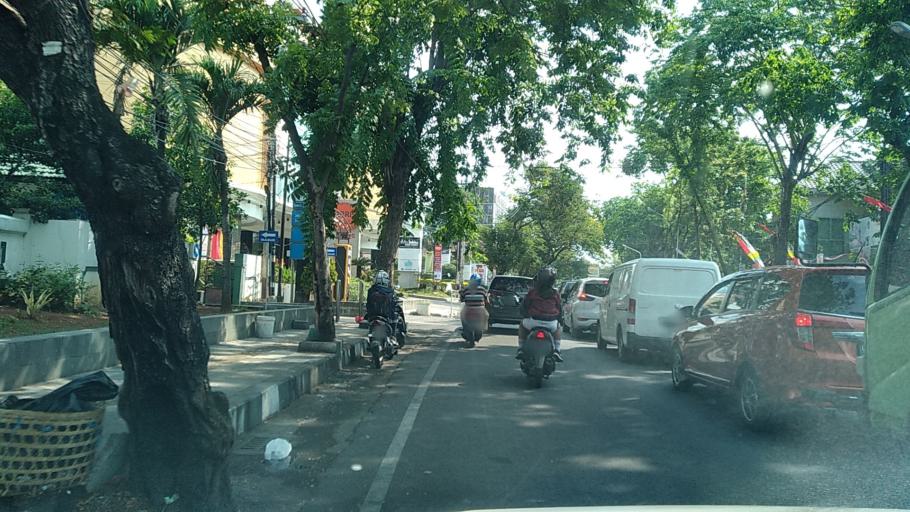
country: ID
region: Central Java
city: Semarang
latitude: -6.9913
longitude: 110.4295
